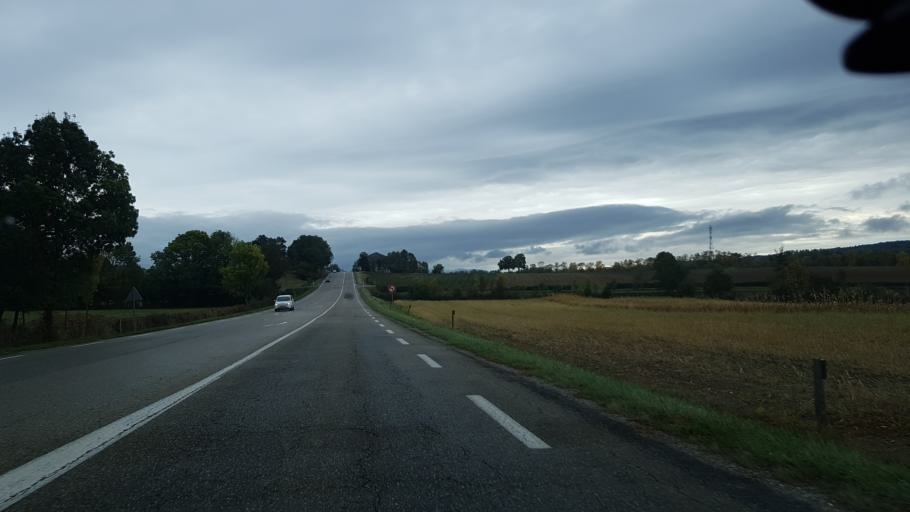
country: FR
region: Rhone-Alpes
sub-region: Departement de l'Ain
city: Saint-Martin-du-Mont
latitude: 46.0774
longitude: 5.3215
